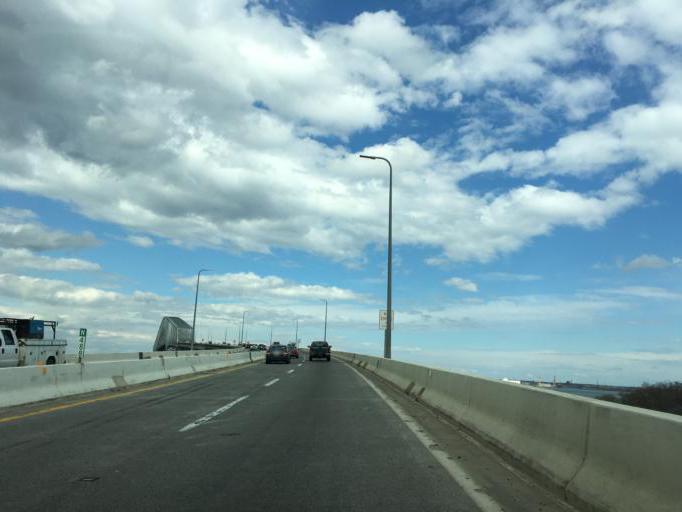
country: US
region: Maryland
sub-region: Baltimore County
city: Dundalk
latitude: 39.2102
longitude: -76.5383
